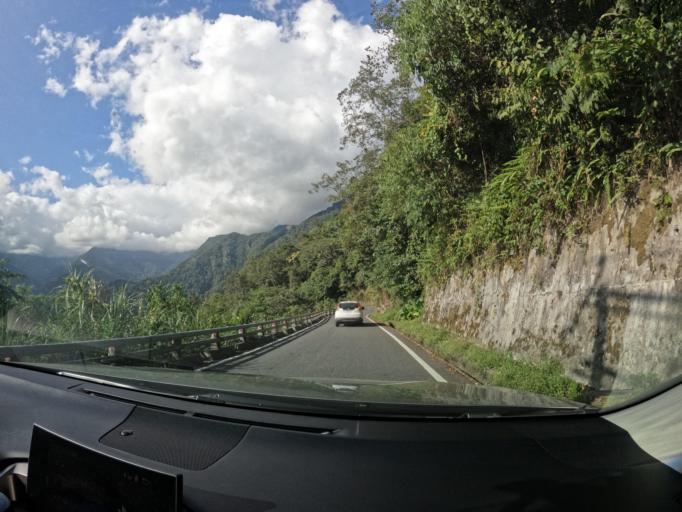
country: TW
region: Taiwan
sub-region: Taitung
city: Taitung
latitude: 23.1944
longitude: 121.0198
